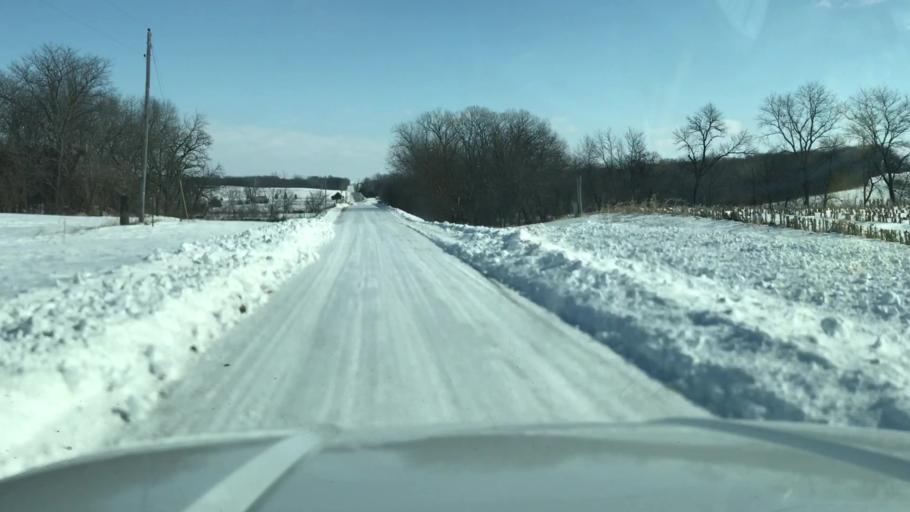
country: US
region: Missouri
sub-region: Nodaway County
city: Maryville
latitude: 40.3865
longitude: -94.6709
